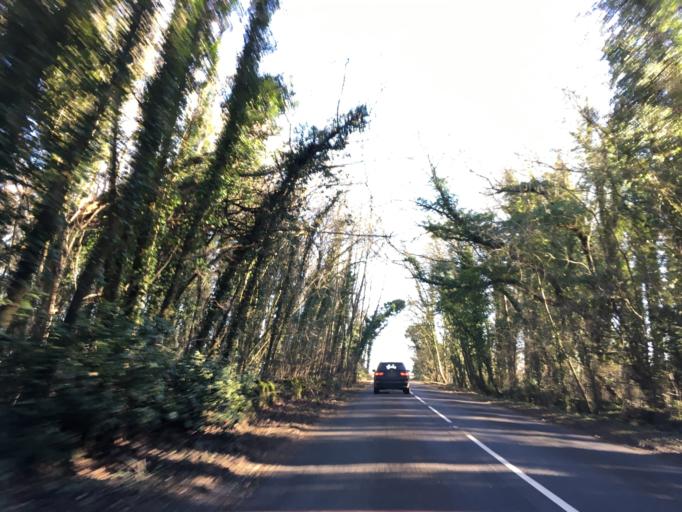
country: GB
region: England
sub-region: Wiltshire
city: Biddestone
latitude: 51.4931
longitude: -2.2061
